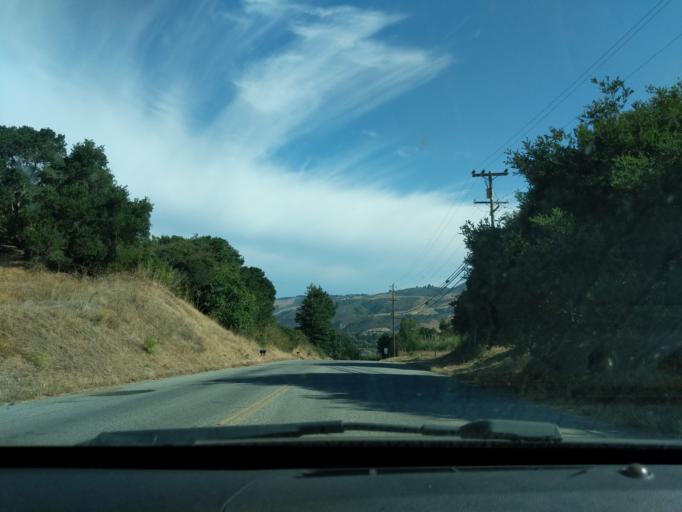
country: US
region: California
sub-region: San Benito County
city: Aromas
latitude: 36.8822
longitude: -121.6418
